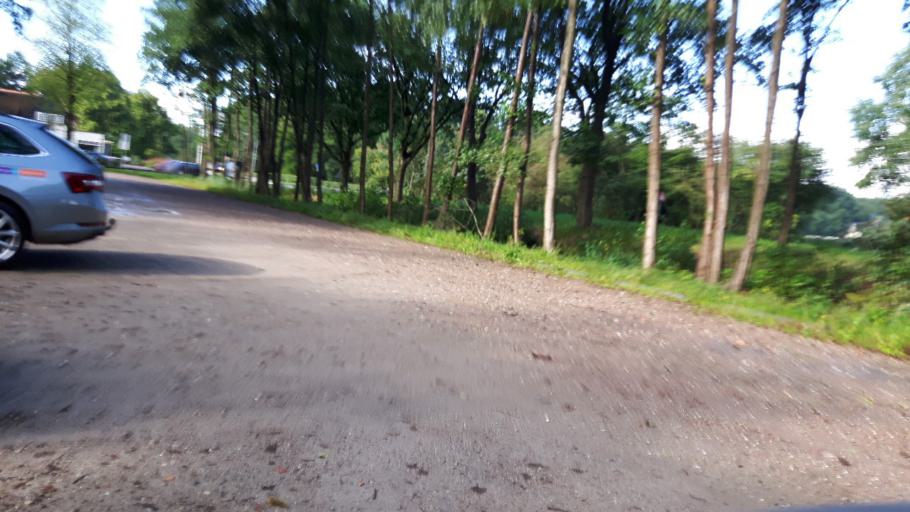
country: NL
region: Friesland
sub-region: Gemeente Smallingerland
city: Drachten
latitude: 53.0675
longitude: 6.1055
